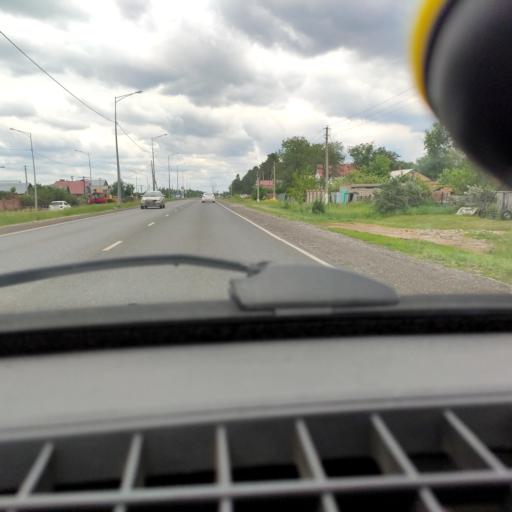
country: RU
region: Samara
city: Povolzhskiy
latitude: 53.5896
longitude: 49.5777
